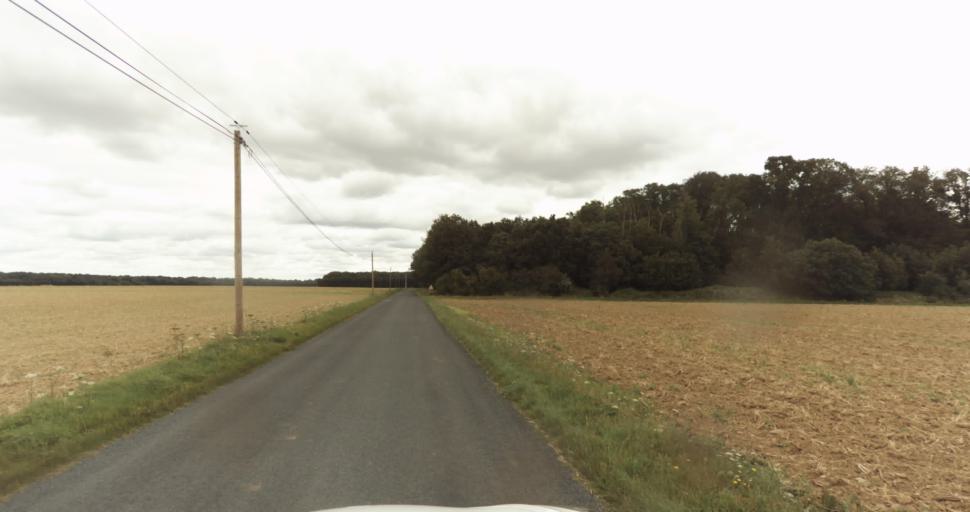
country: FR
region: Haute-Normandie
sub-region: Departement de l'Eure
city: La Madeleine-de-Nonancourt
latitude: 48.8223
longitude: 1.2119
